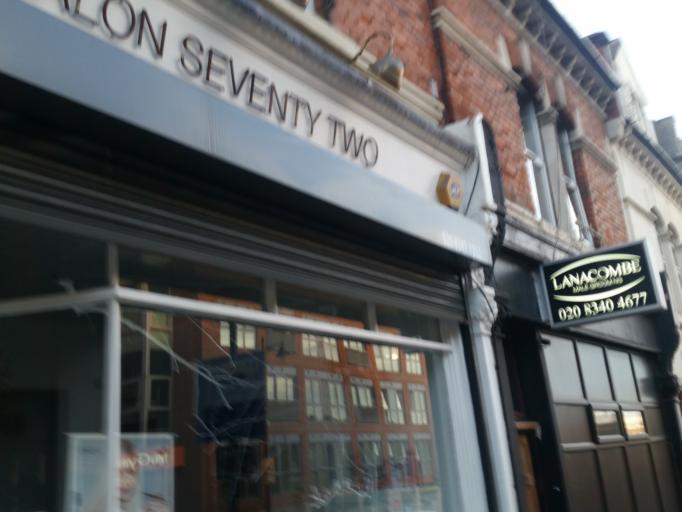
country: GB
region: England
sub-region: Greater London
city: Crouch End
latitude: 51.5771
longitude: -0.1254
